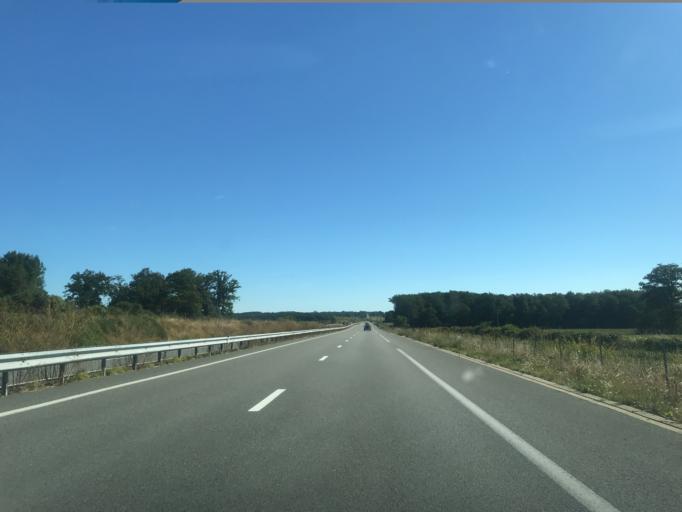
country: FR
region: Limousin
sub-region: Departement de la Creuse
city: Gouzon
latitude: 46.2086
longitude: 2.2731
